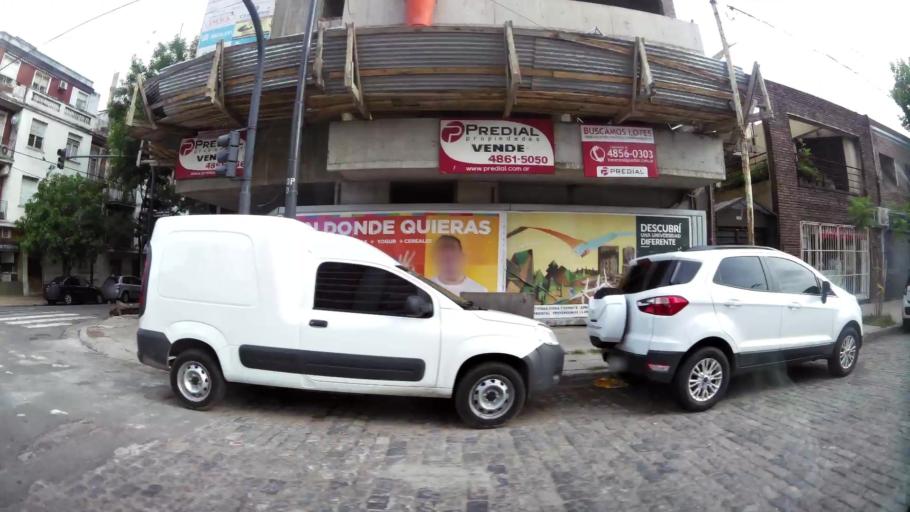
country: AR
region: Buenos Aires F.D.
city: Villa Santa Rita
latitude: -34.6338
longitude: -58.4703
